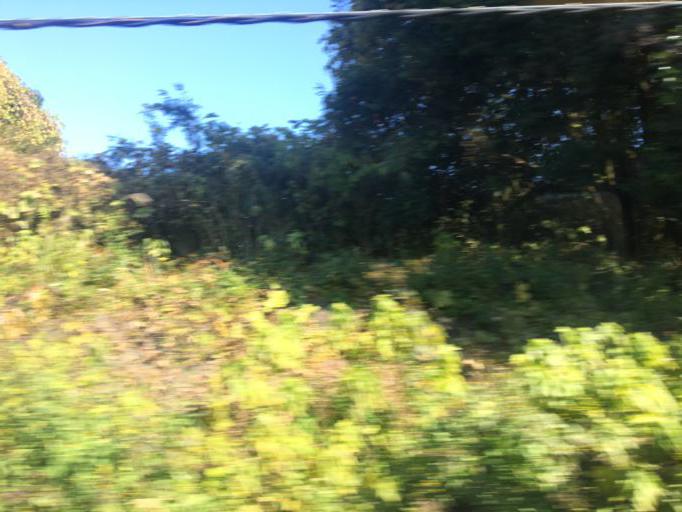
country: JP
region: Tochigi
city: Oyama
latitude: 36.3322
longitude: 139.8070
